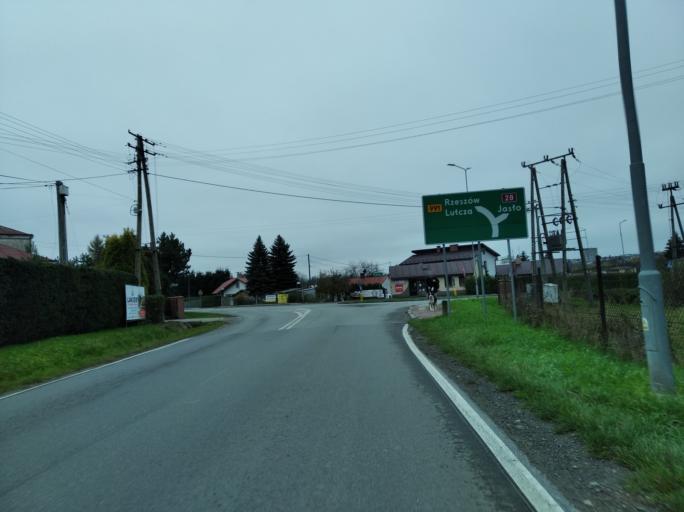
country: PL
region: Subcarpathian Voivodeship
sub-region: Krosno
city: Krosno
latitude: 49.7072
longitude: 21.7588
